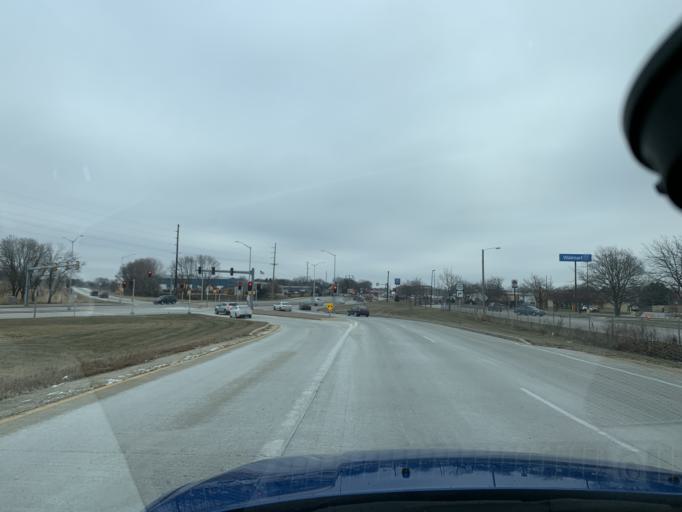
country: US
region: Wisconsin
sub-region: Dane County
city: Sun Prairie
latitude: 43.1753
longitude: -89.2492
